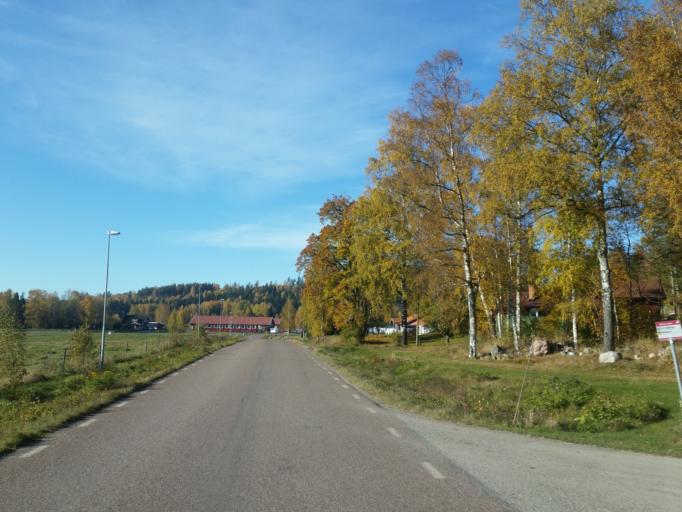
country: SE
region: Dalarna
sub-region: Borlange Kommun
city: Ornas
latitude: 60.4470
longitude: 15.6320
